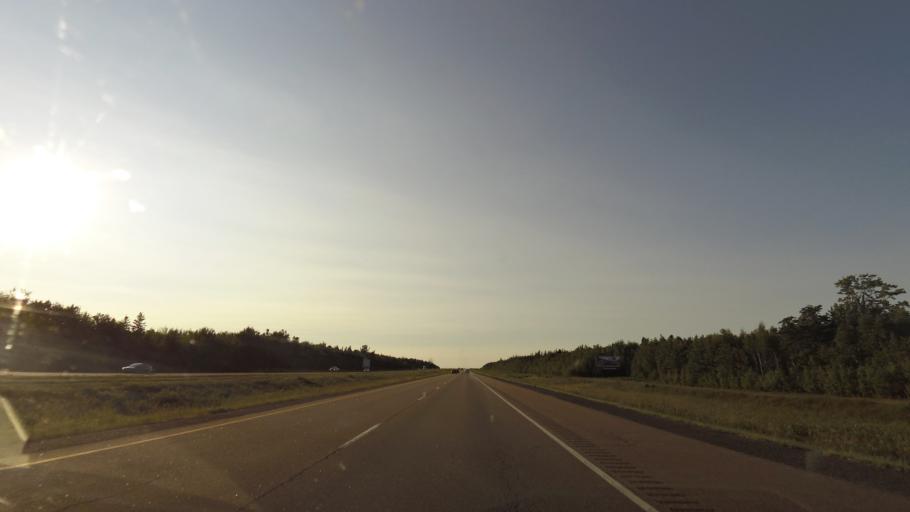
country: CA
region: New Brunswick
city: Dieppe
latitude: 46.1157
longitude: -64.6216
